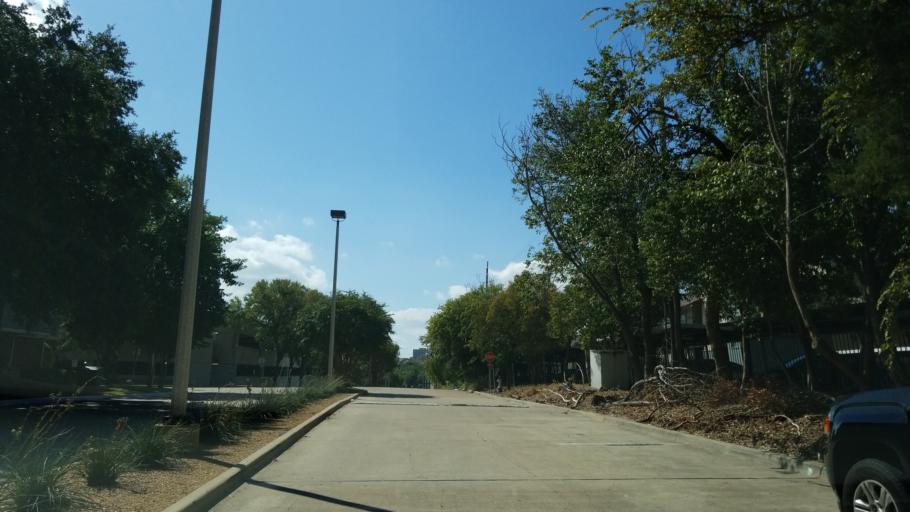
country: US
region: Texas
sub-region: Dallas County
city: Addison
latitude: 32.9504
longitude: -96.8065
